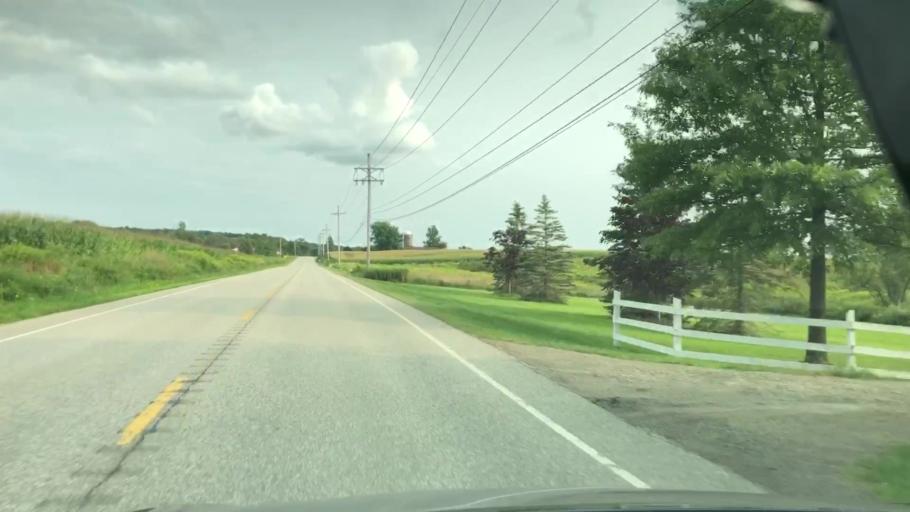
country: US
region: Pennsylvania
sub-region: Erie County
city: Union City
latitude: 41.9483
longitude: -79.8480
